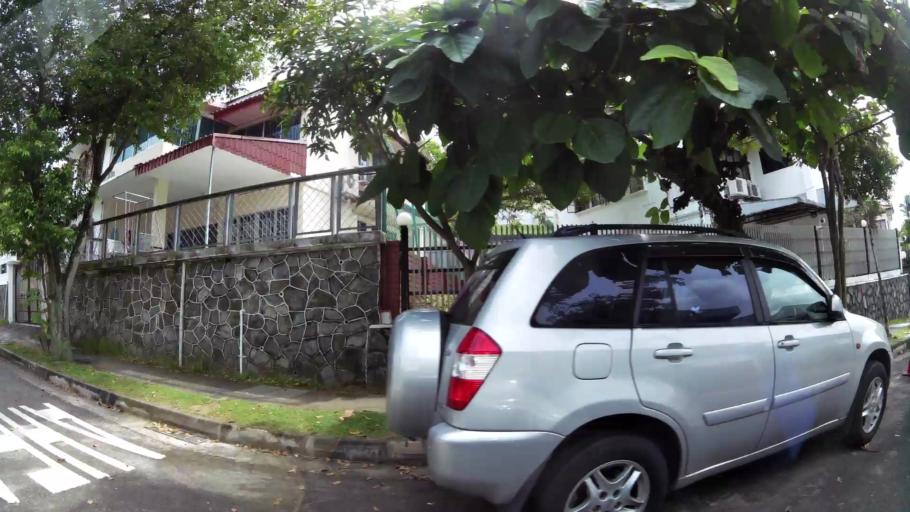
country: SG
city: Singapore
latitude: 1.3442
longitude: 103.7707
